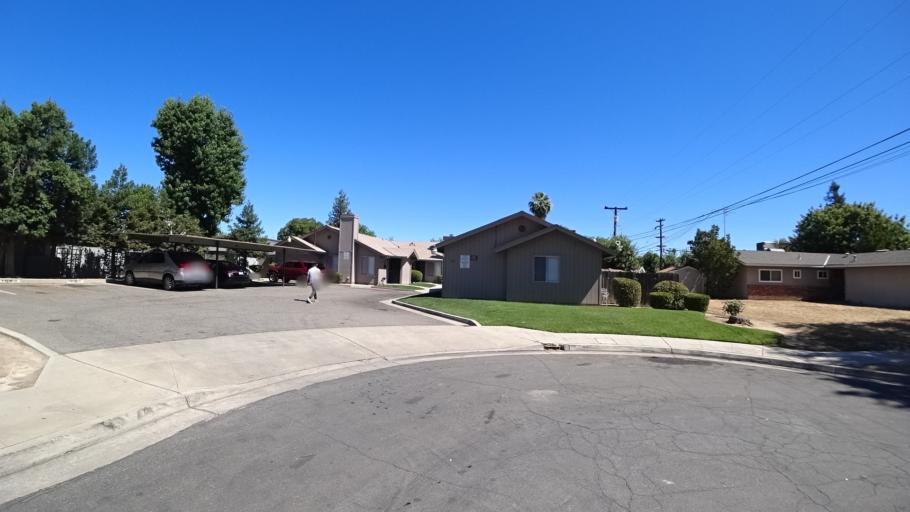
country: US
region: California
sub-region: Fresno County
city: West Park
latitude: 36.7969
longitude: -119.8490
